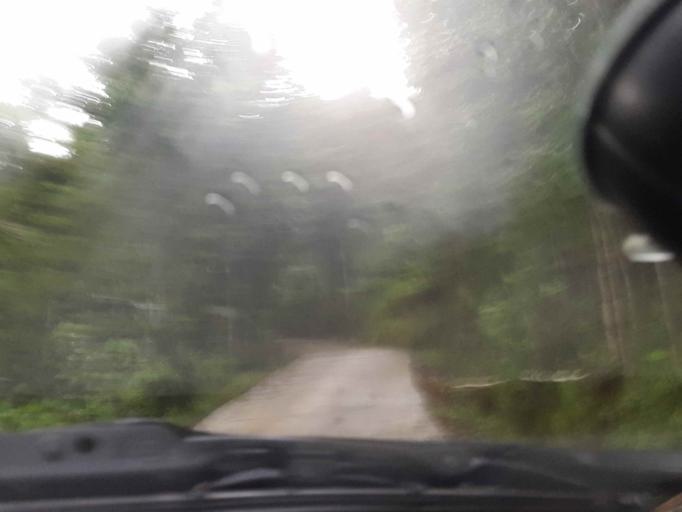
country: ID
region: Central Java
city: Wonosobo
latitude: -7.5219
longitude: 109.8083
